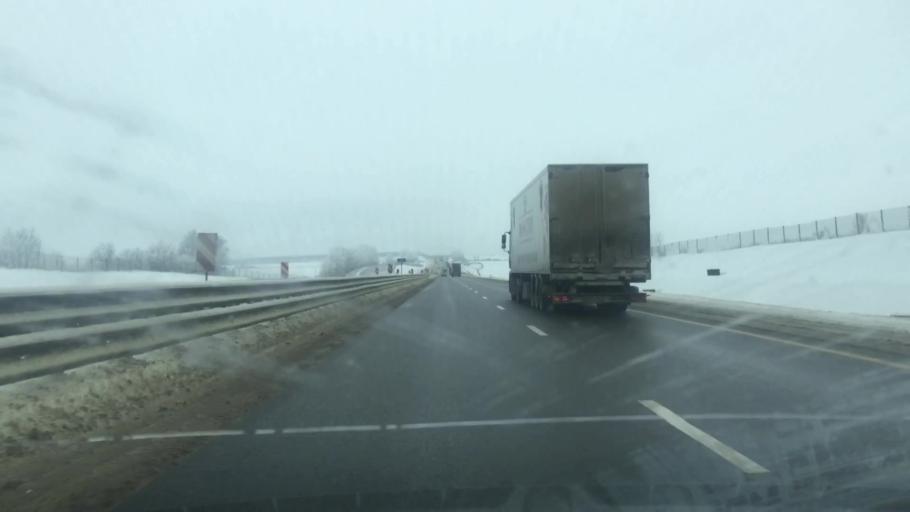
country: RU
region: Tula
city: Kazachka
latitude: 53.3339
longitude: 38.1806
